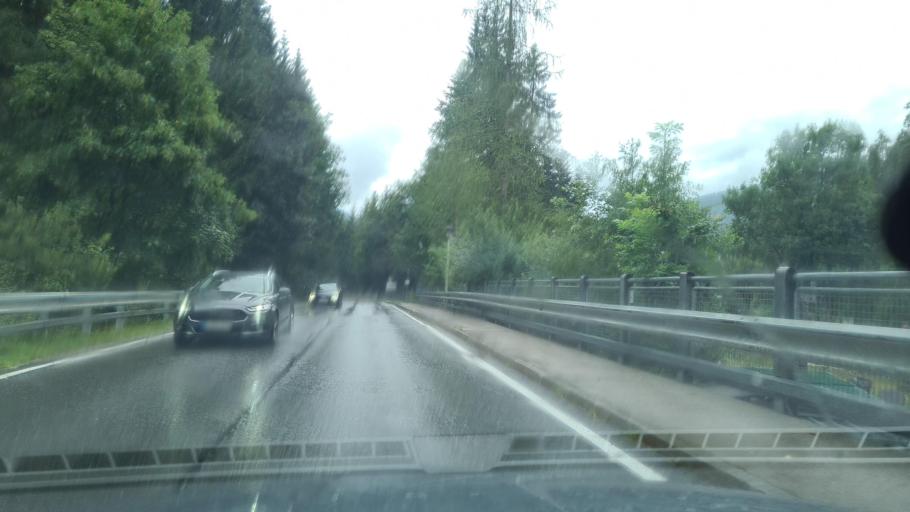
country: AT
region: Salzburg
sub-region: Politischer Bezirk Sankt Johann im Pongau
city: Altenmarkt im Pongau
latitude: 47.3643
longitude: 13.4251
